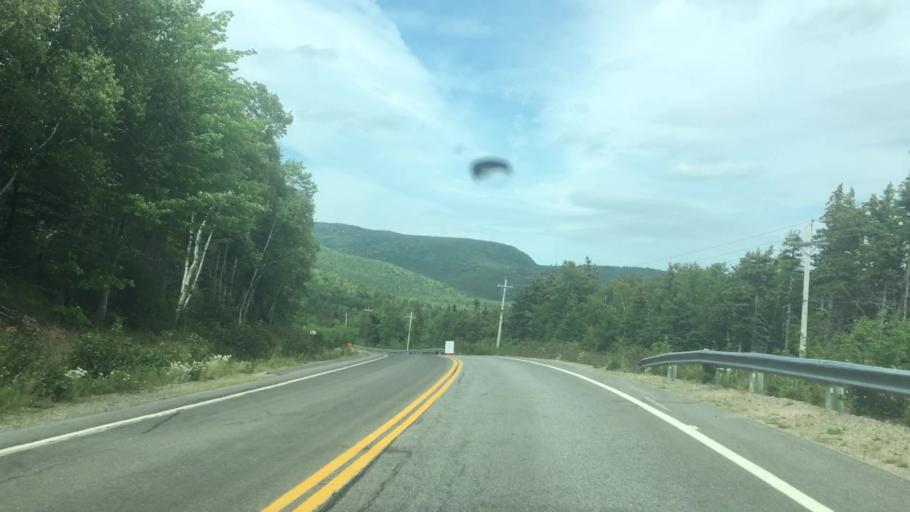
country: CA
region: Nova Scotia
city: Sydney Mines
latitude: 46.5406
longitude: -60.4140
